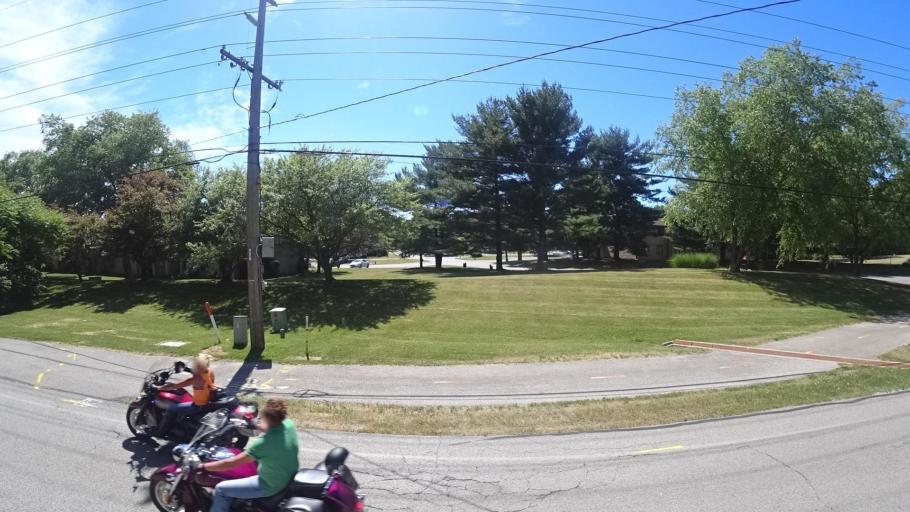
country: US
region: Indiana
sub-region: Porter County
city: Porter
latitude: 41.6259
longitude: -87.0673
